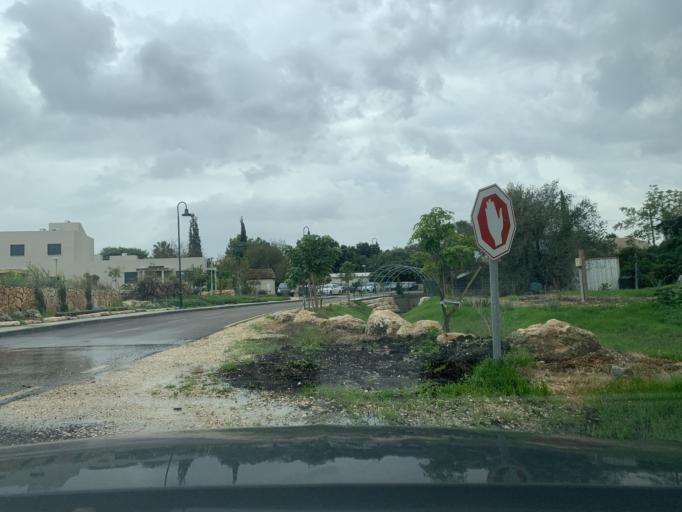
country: PS
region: West Bank
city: Qalqilyah
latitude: 32.2131
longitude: 34.9767
